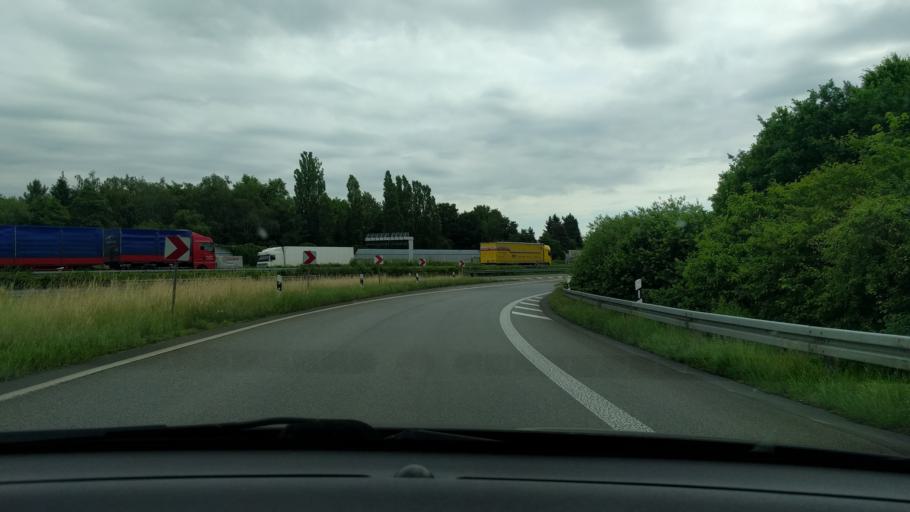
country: DE
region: North Rhine-Westphalia
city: Waltrop
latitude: 51.5849
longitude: 7.3698
